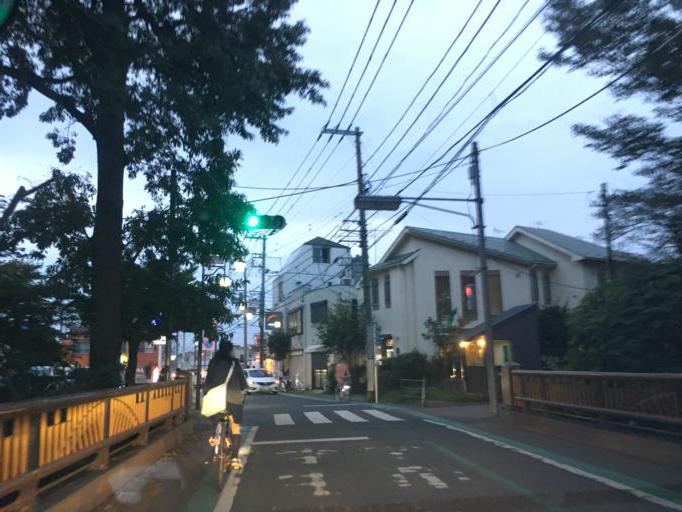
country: JP
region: Tokyo
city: Kokubunji
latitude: 35.7225
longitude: 139.4572
